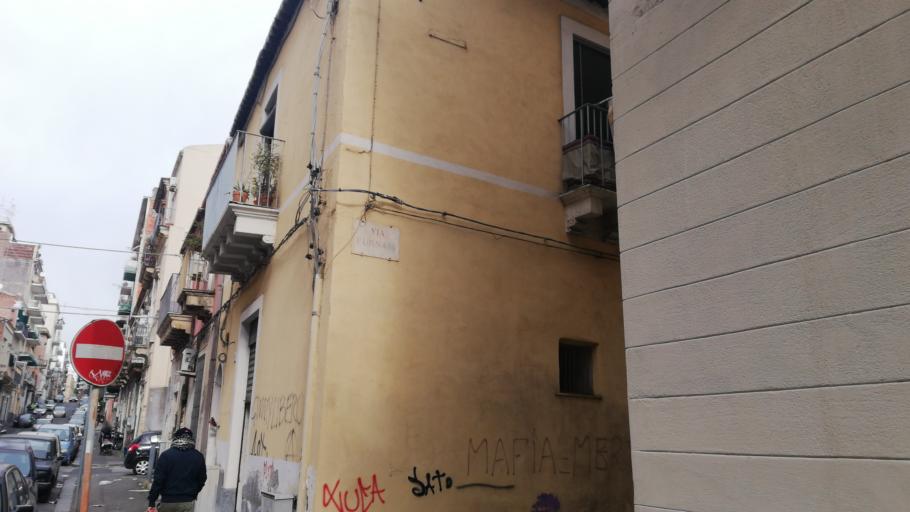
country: IT
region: Sicily
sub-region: Catania
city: Canalicchio
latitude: 37.5186
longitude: 15.0844
